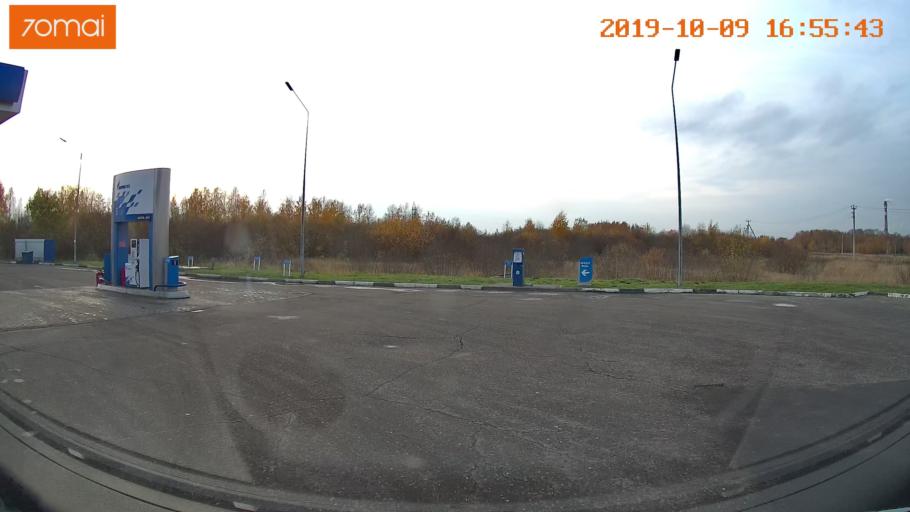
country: RU
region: Ivanovo
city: Privolzhsk
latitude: 57.3672
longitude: 41.2727
